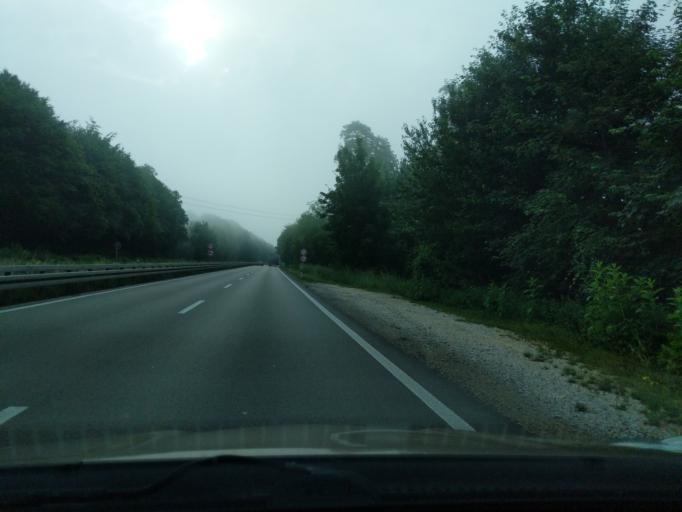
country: DE
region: Bavaria
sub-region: Swabia
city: Diedorf
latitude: 48.3705
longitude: 10.8072
